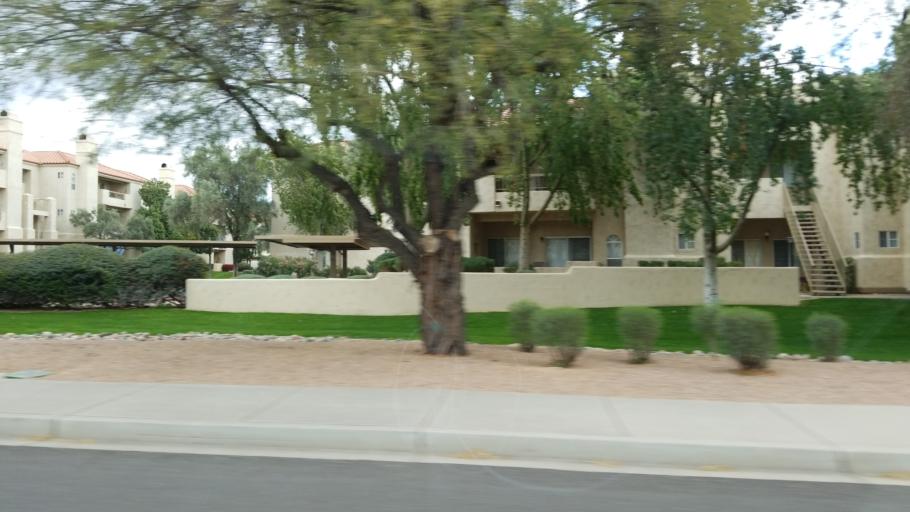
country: US
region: Arizona
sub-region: Maricopa County
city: Paradise Valley
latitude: 33.6140
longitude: -111.8783
